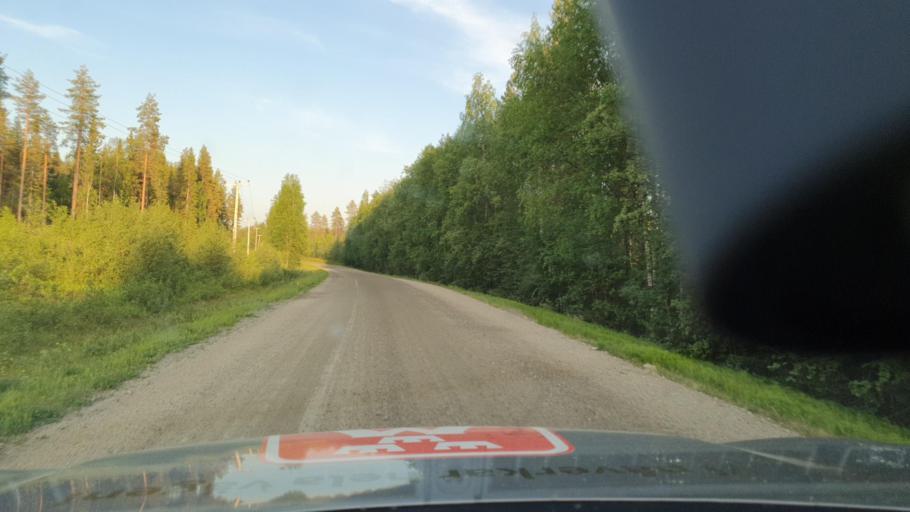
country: SE
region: Norrbotten
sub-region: Bodens Kommun
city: Boden
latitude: 66.1647
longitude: 21.5400
